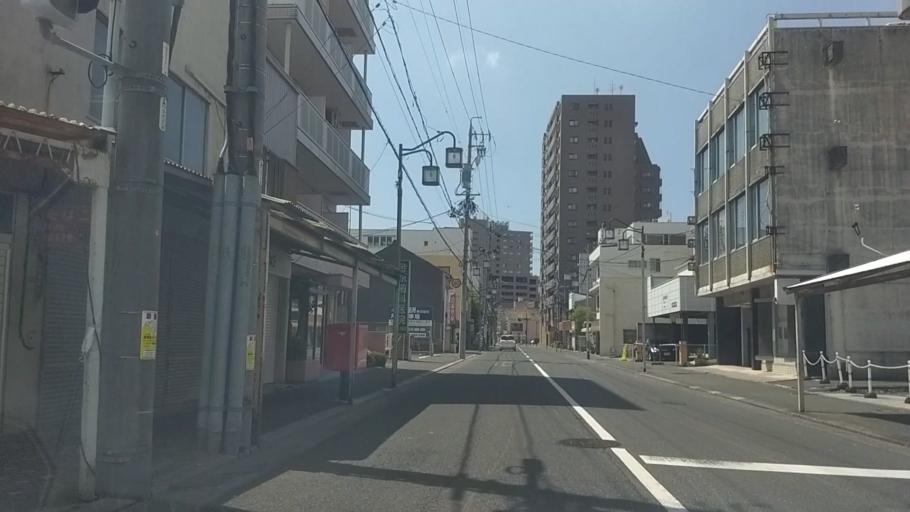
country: JP
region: Shizuoka
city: Hamamatsu
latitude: 34.7118
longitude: 137.7301
